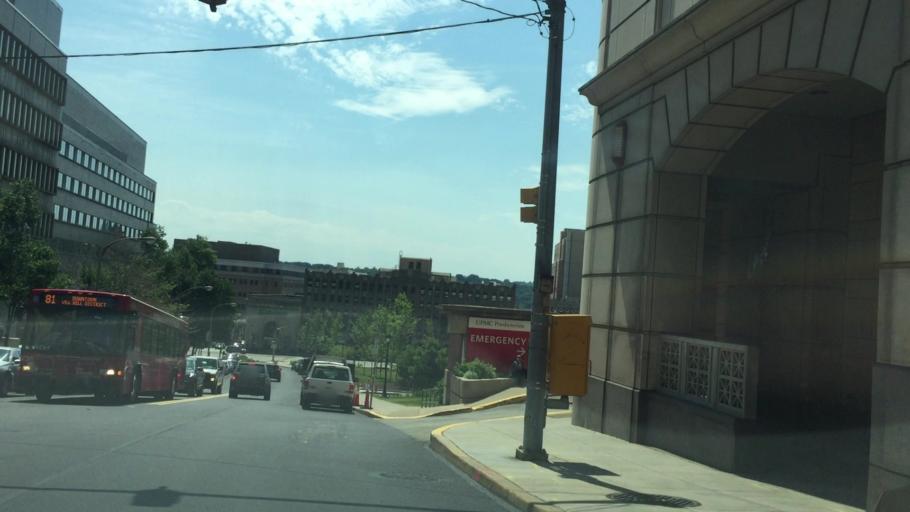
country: US
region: Pennsylvania
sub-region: Allegheny County
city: Bloomfield
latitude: 40.4432
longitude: -79.9600
